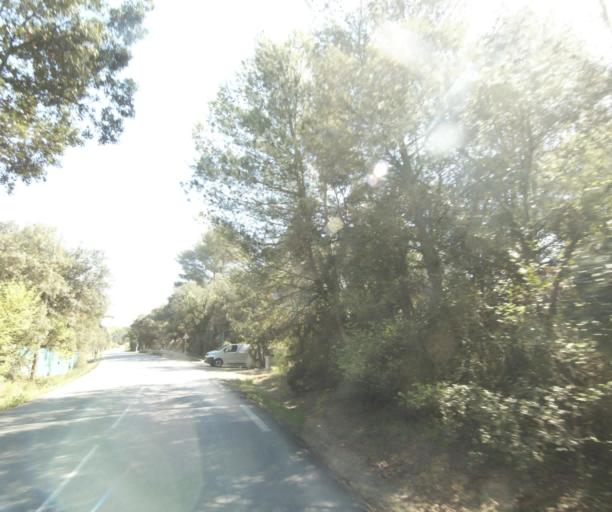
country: FR
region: Languedoc-Roussillon
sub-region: Departement de l'Herault
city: Sussargues
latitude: 43.7022
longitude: 4.0074
